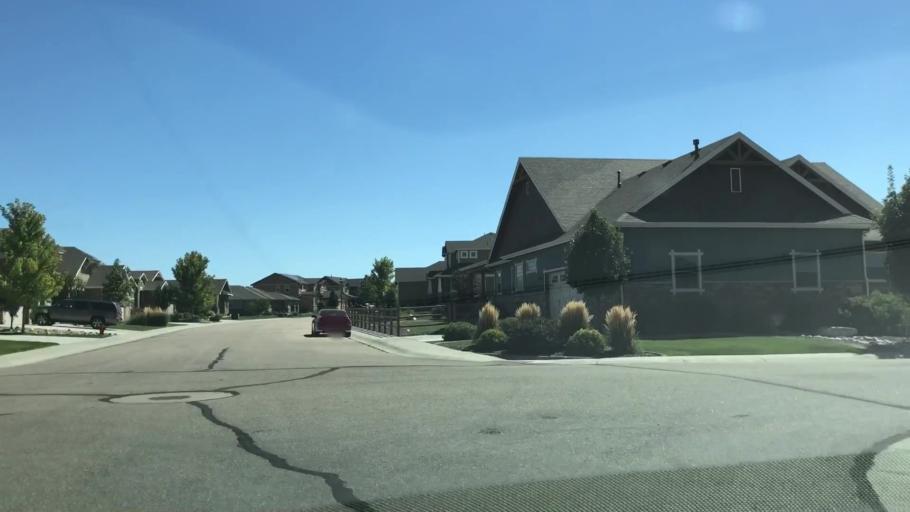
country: US
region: Colorado
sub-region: Weld County
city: Windsor
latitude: 40.4542
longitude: -104.9582
